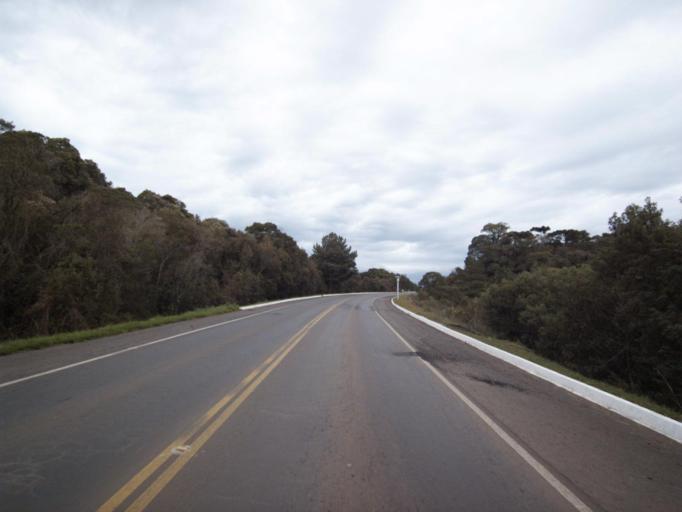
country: BR
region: Santa Catarina
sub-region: Concordia
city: Concordia
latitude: -26.9683
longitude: -51.8513
